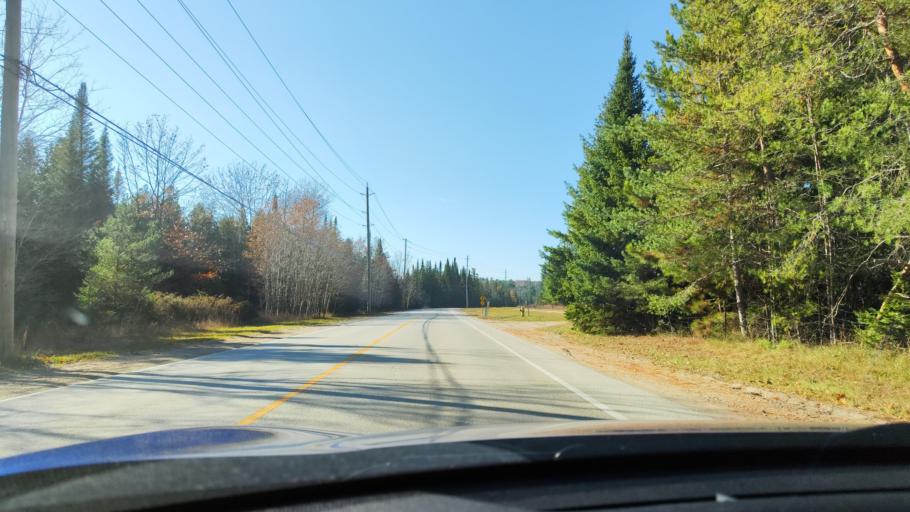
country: CA
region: Ontario
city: Wasaga Beach
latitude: 44.4999
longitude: -79.9925
